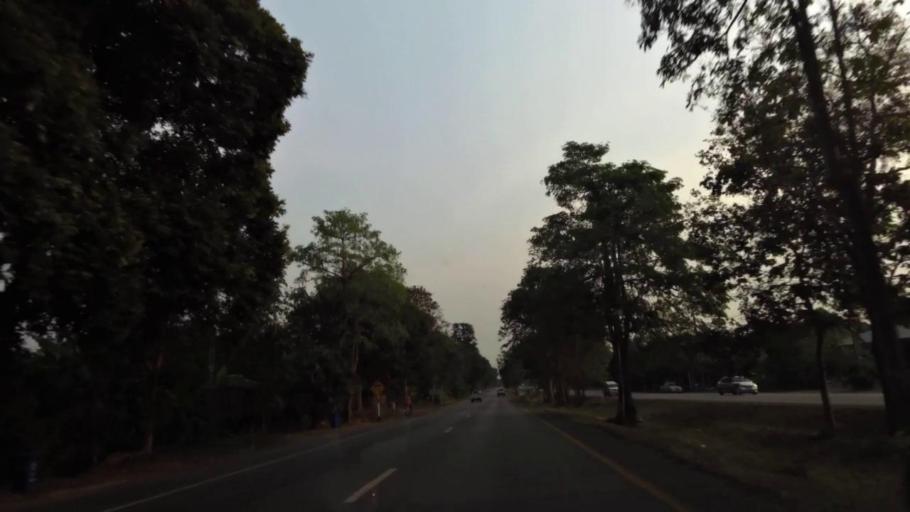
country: TH
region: Chanthaburi
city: Khlung
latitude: 12.4928
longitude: 102.1734
